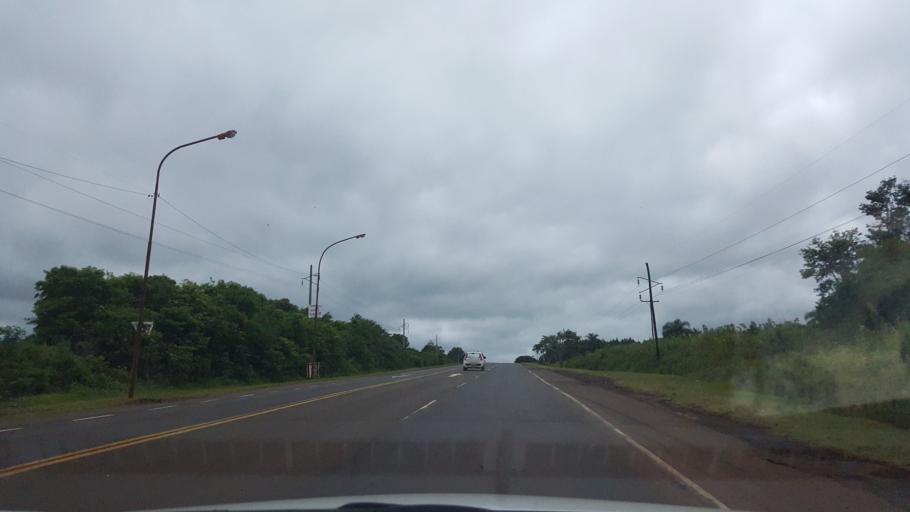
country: AR
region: Misiones
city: Capiovi
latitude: -26.9529
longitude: -55.0948
